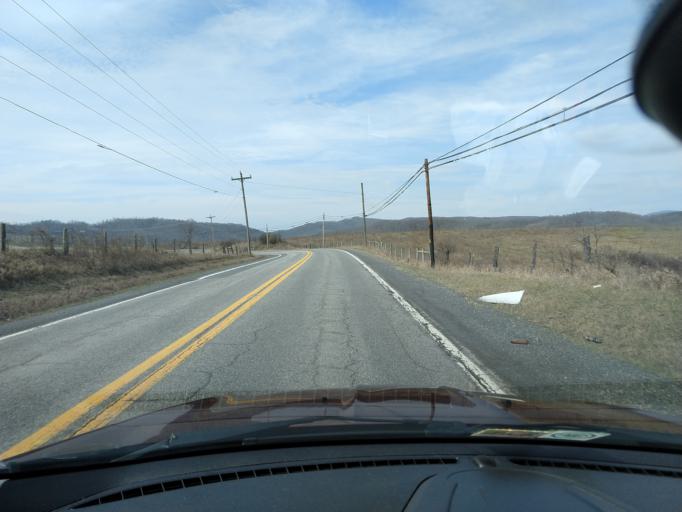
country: US
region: West Virginia
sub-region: Greenbrier County
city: Lewisburg
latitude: 37.9005
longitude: -80.4017
